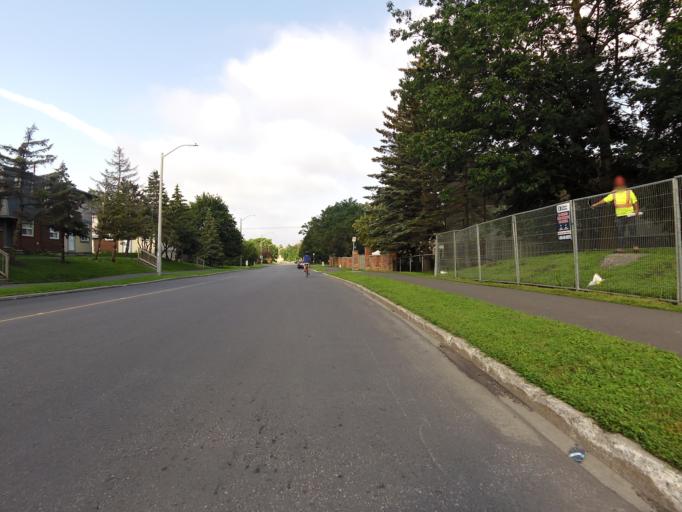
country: CA
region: Ontario
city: Ottawa
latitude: 45.3495
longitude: -75.6776
